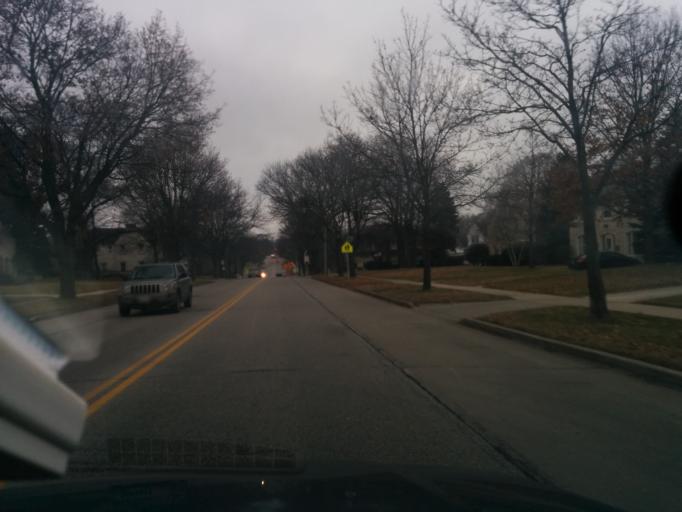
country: US
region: Wisconsin
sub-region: Milwaukee County
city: Wauwatosa
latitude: 43.0388
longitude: -88.0099
